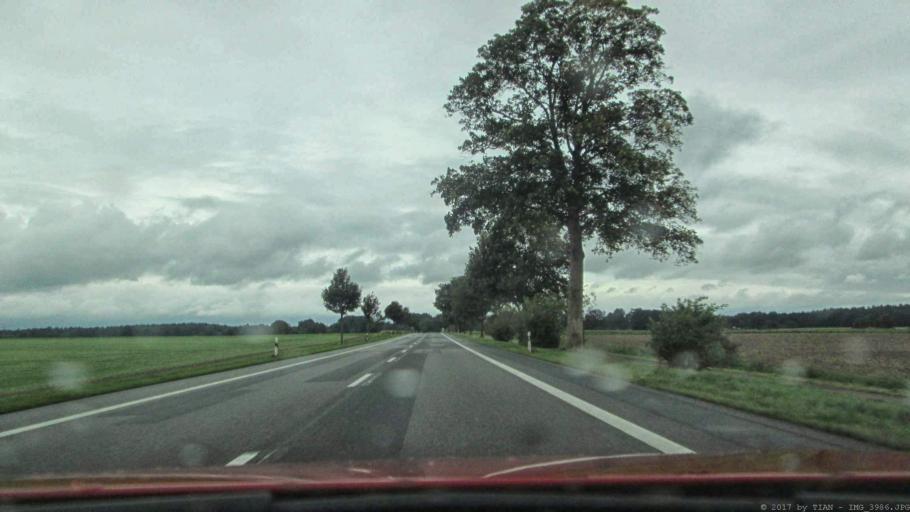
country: DE
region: Lower Saxony
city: Jelmstorf
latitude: 53.0932
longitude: 10.5256
